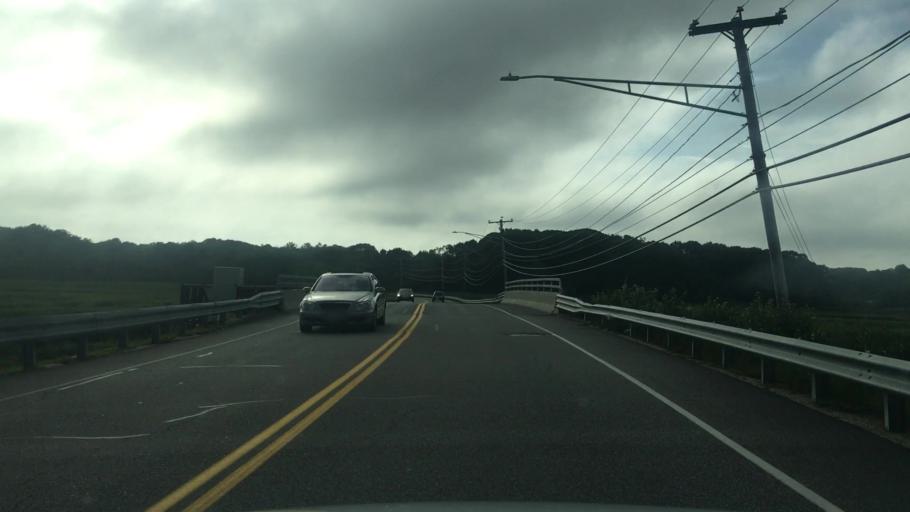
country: US
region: Maine
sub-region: Cumberland County
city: Scarborough
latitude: 43.5798
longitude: -70.3258
